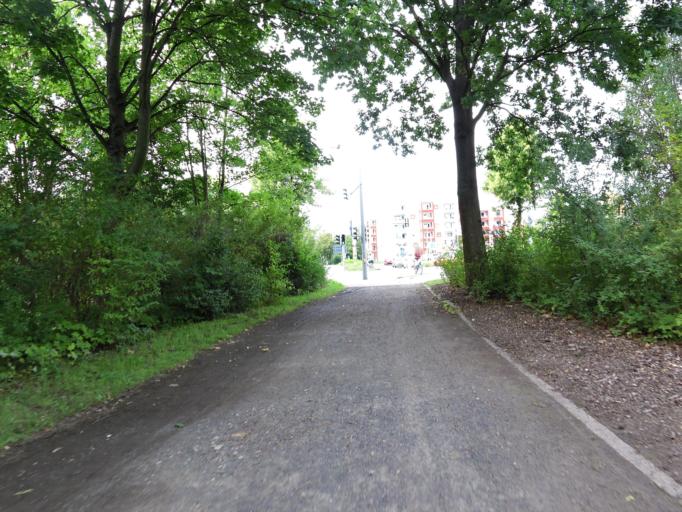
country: DE
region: Saxony
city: Leipzig
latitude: 51.3513
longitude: 12.4220
